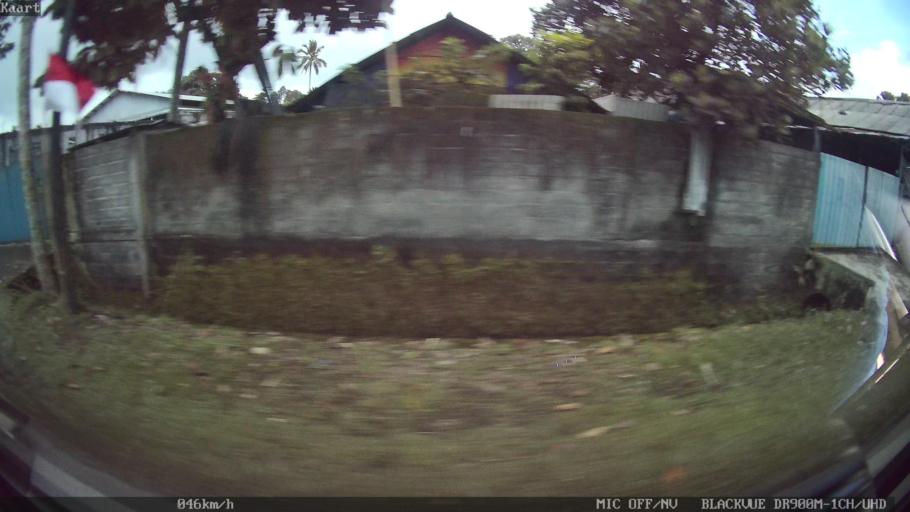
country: ID
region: Bali
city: Pohgending Kawan
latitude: -8.4503
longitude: 115.1396
